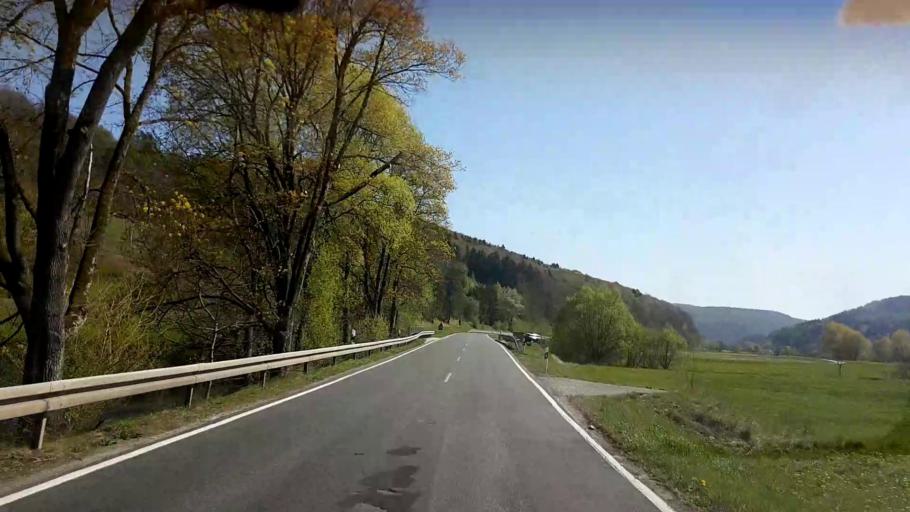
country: DE
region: Bavaria
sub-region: Upper Franconia
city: Unterleinleiter
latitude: 49.8164
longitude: 11.1926
